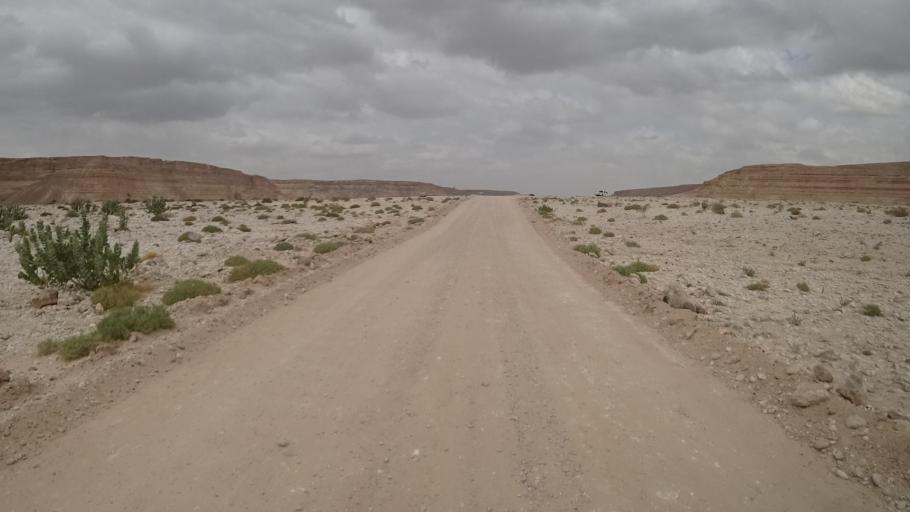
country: YE
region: Al Mahrah
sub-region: Shahan
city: Shihan as Sufla
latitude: 17.4716
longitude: 53.0002
